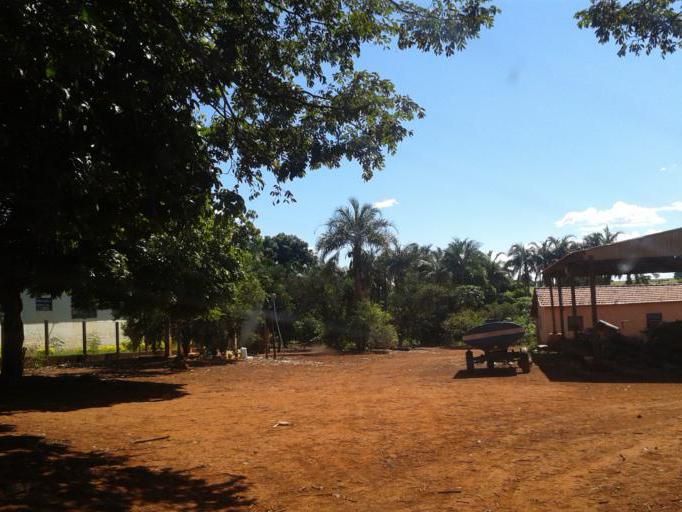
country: BR
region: Minas Gerais
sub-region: Capinopolis
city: Capinopolis
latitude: -18.6505
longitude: -49.5723
